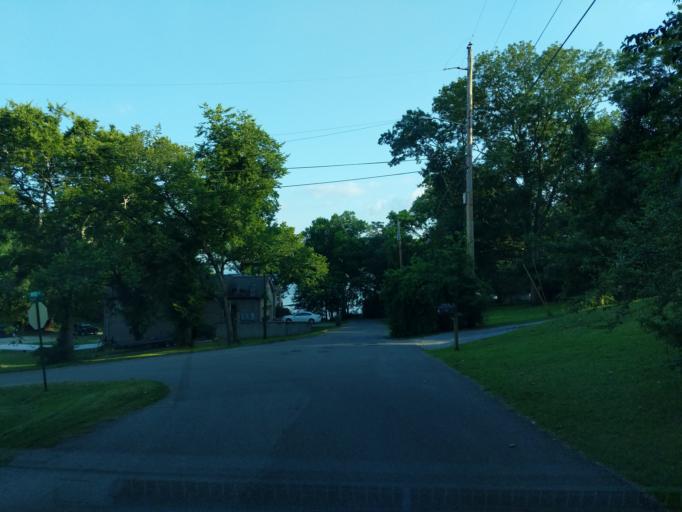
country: US
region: Tennessee
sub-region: Sumner County
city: Hendersonville
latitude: 36.2956
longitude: -86.6446
